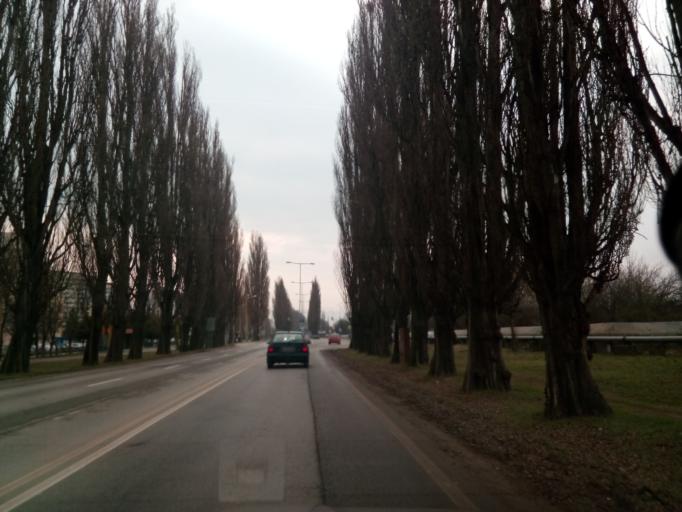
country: SK
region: Kosicky
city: Kosice
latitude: 48.6837
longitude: 21.2885
